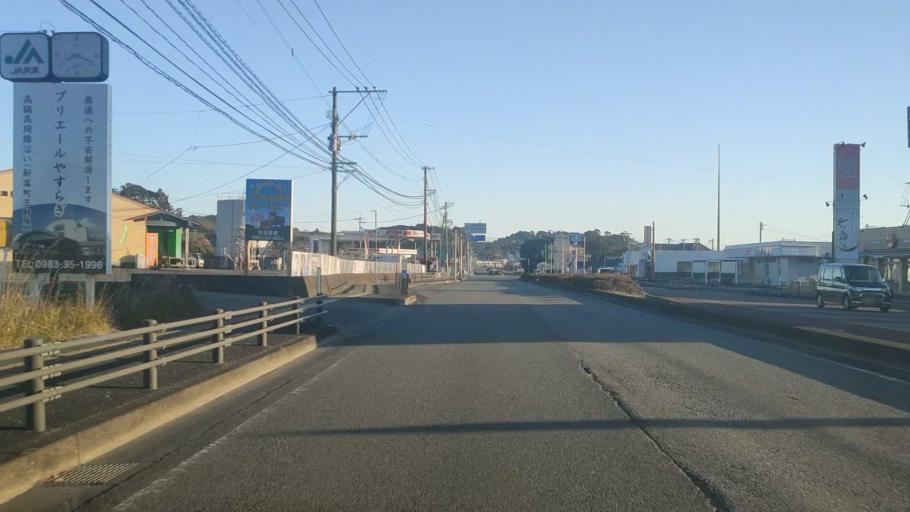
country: JP
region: Miyazaki
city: Takanabe
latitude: 32.0693
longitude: 131.4894
